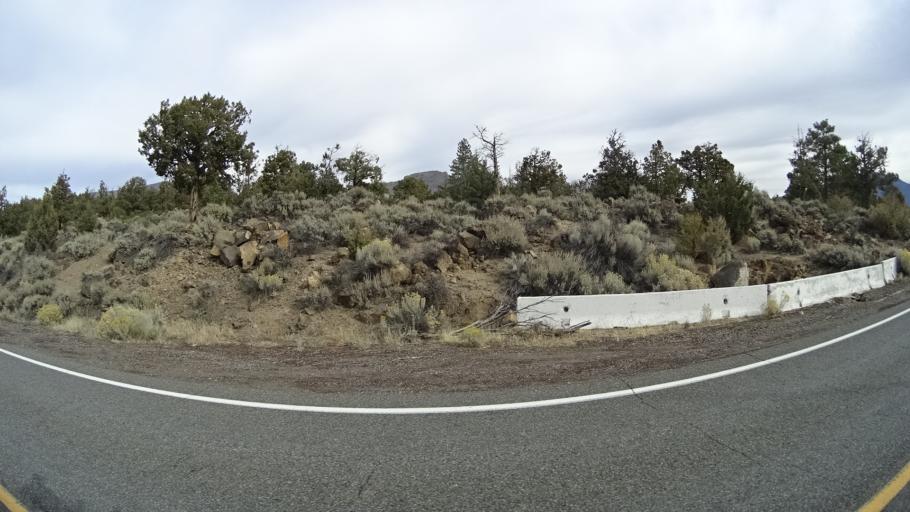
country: US
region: California
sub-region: Siskiyou County
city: Weed
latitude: 41.5585
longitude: -122.2575
